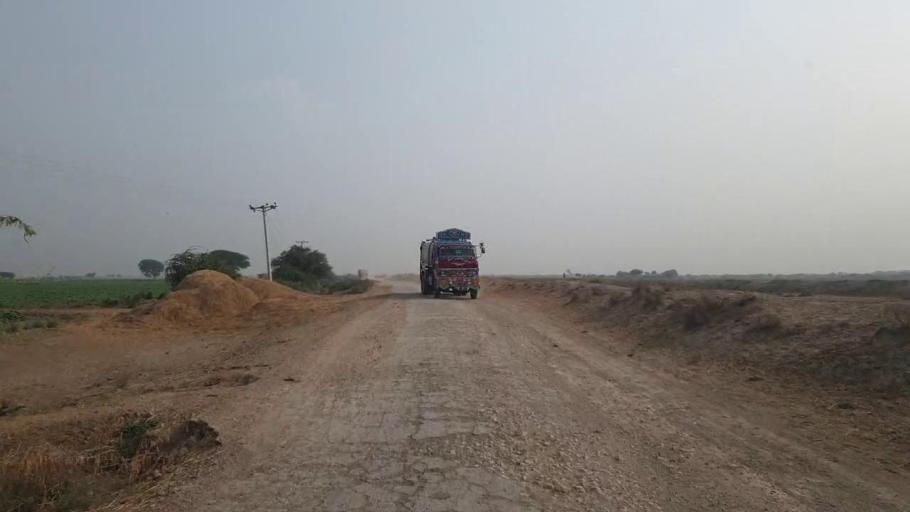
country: PK
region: Sindh
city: Mirpur Batoro
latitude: 24.5704
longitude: 68.3984
